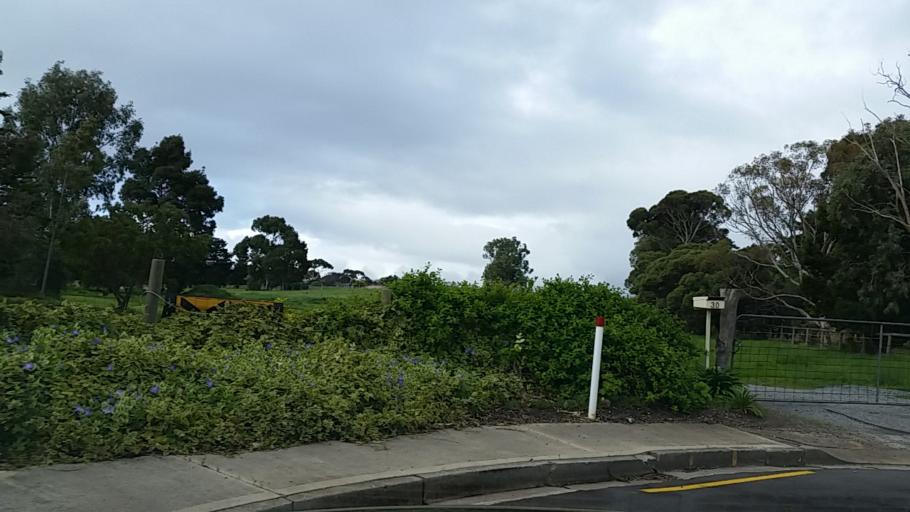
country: AU
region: South Australia
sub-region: Marion
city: Trott Park
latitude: -35.0631
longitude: 138.5382
